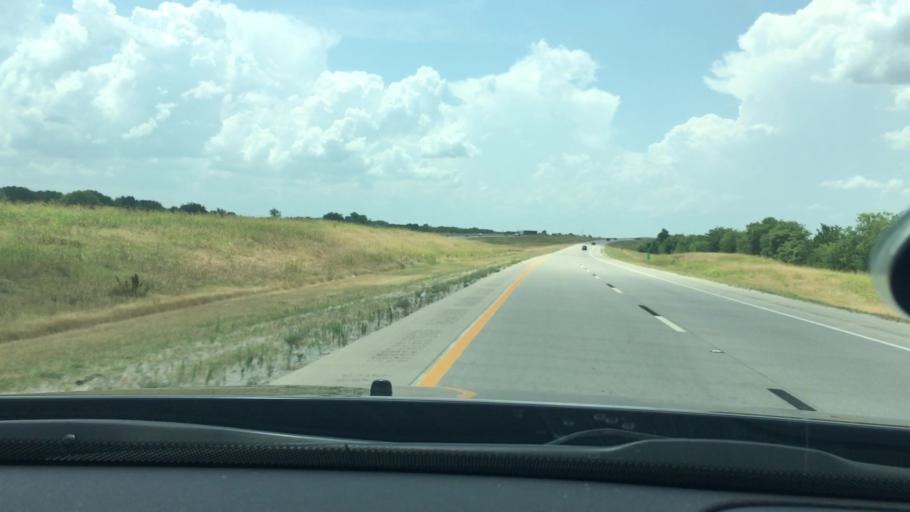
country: US
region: Oklahoma
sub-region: Carter County
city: Ardmore
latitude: 34.1092
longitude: -97.1525
